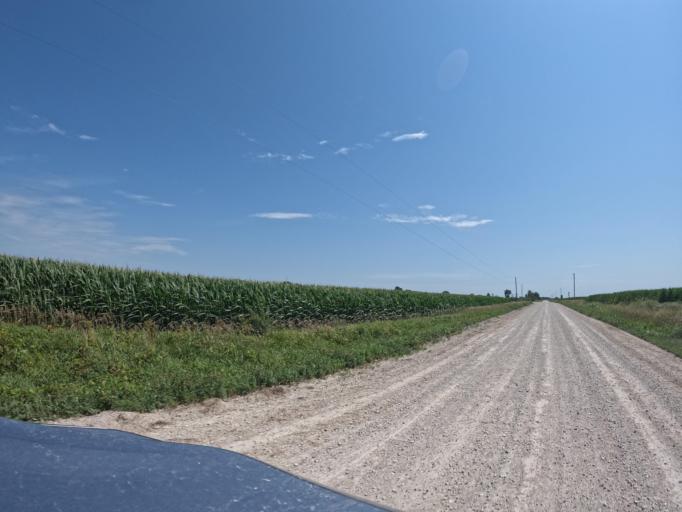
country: US
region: Iowa
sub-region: Henry County
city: Mount Pleasant
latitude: 40.8947
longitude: -91.6318
